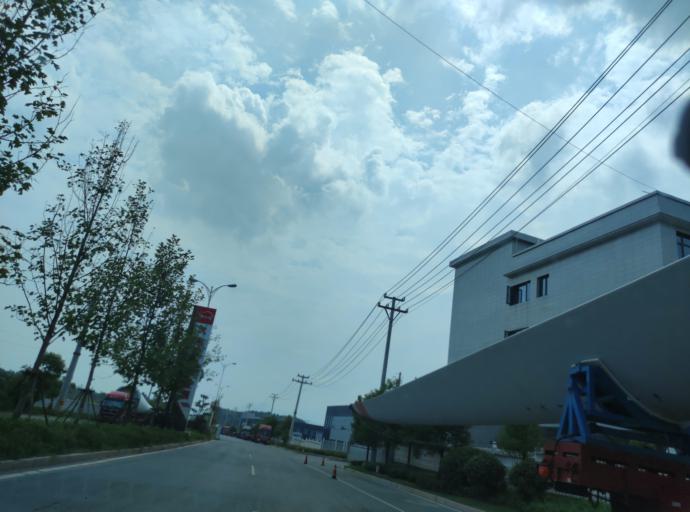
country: CN
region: Jiangxi Sheng
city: Yuannan
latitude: 27.6641
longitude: 114.0205
